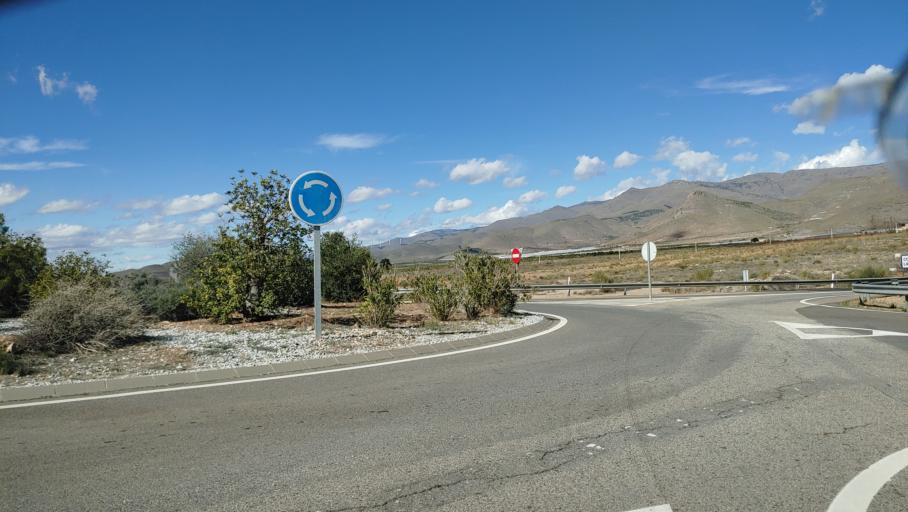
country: ES
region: Andalusia
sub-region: Provincia de Almeria
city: Gergal
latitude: 37.1178
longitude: -2.5915
